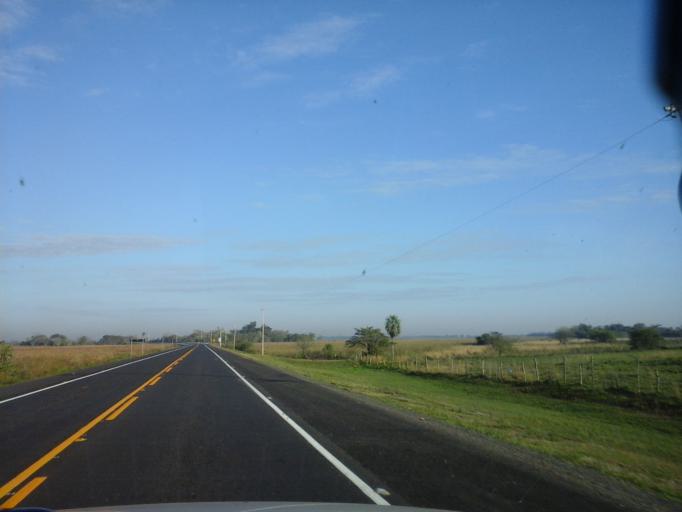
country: PY
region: Neembucu
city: Cerrito
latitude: -26.8654
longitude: -57.5847
